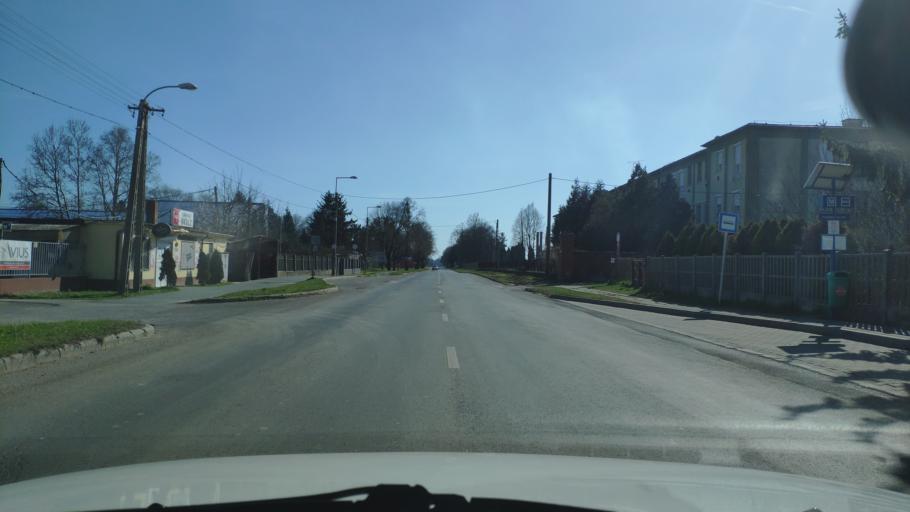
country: HU
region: Zala
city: Nagykanizsa
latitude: 46.4309
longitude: 16.9873
